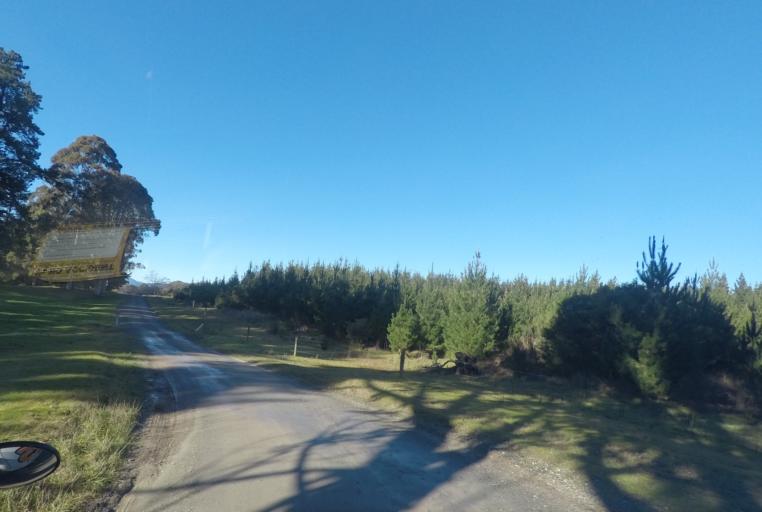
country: NZ
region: Tasman
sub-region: Tasman District
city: Mapua
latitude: -41.2646
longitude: 173.1427
